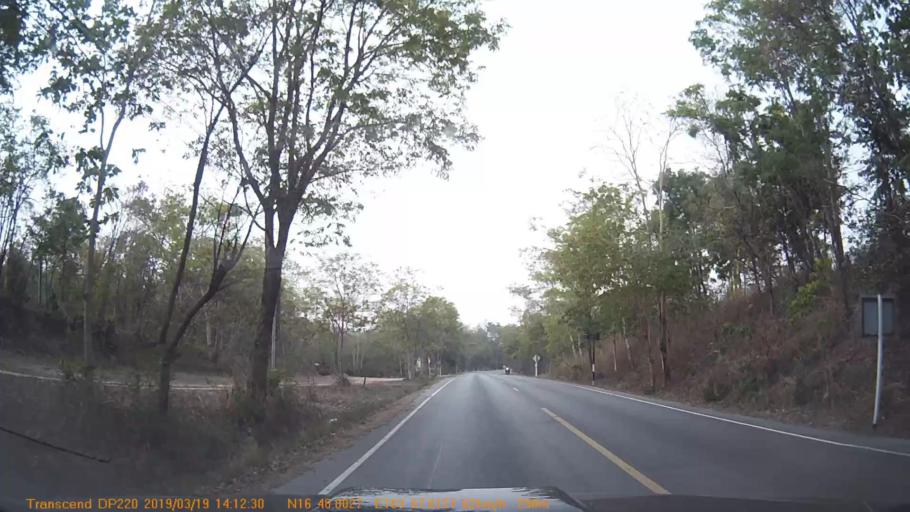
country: TH
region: Kalasin
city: Na Khu
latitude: 16.8138
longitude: 103.9599
